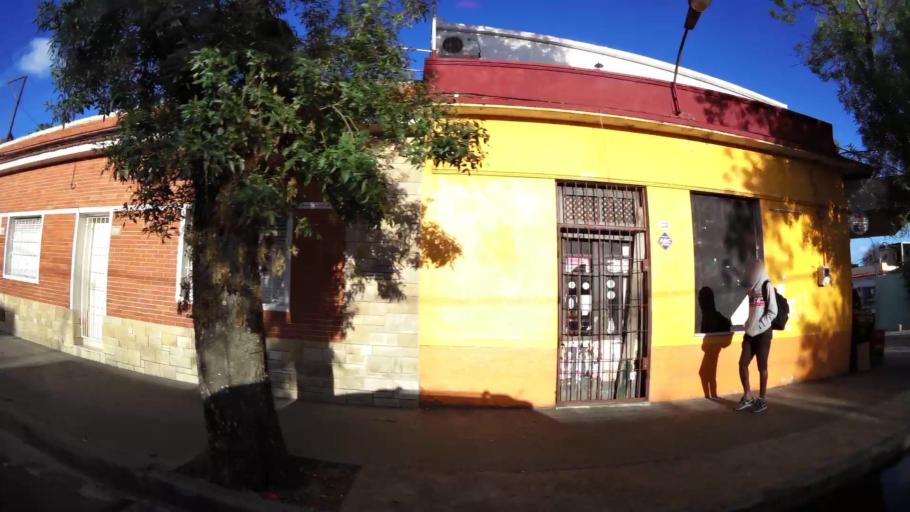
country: UY
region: Montevideo
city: Montevideo
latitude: -34.8920
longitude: -56.2499
